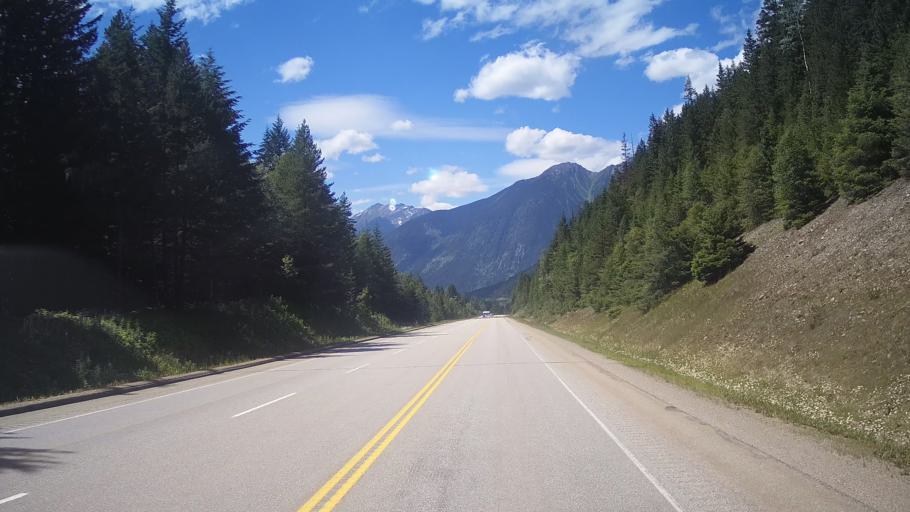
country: CA
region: Alberta
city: Grande Cache
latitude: 53.0253
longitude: -119.1549
